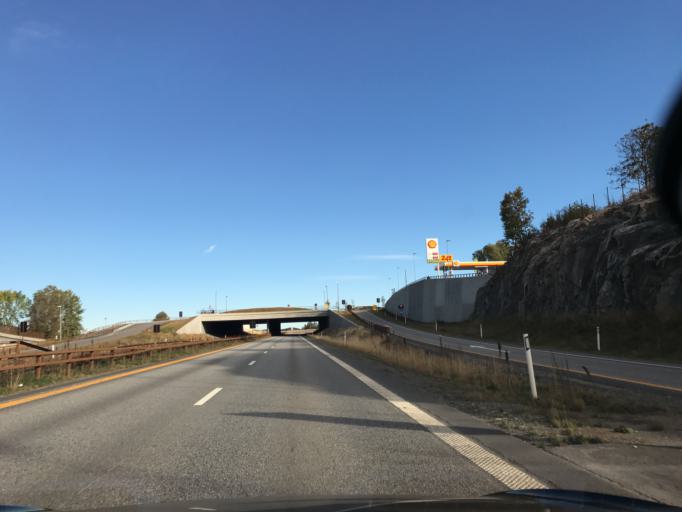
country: NO
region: Hedmark
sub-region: Stange
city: Stange
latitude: 60.5612
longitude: 11.2547
